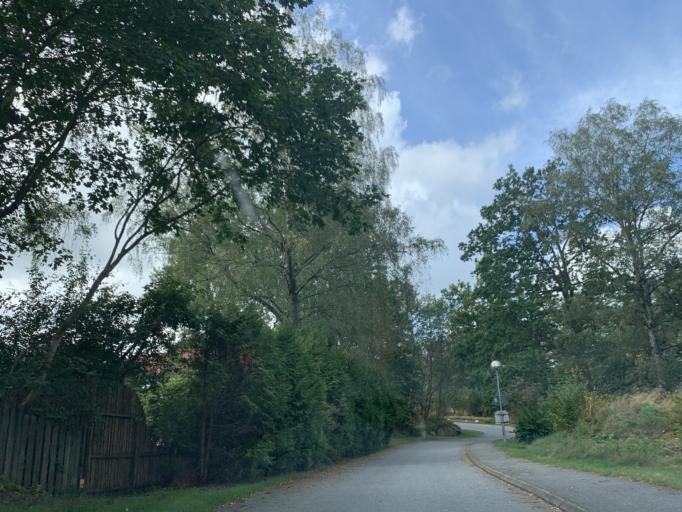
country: SE
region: Vaestra Goetaland
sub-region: Goteborg
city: Eriksbo
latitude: 57.7656
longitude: 12.0447
